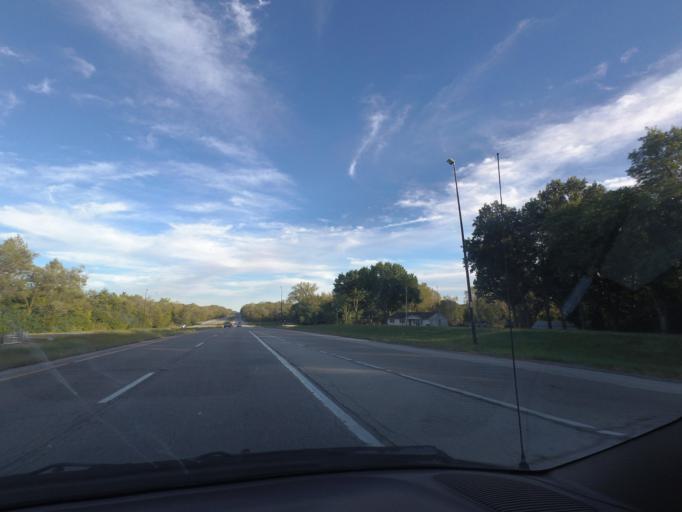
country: US
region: Illinois
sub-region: Sangamon County
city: Grandview
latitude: 39.7845
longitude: -89.5966
